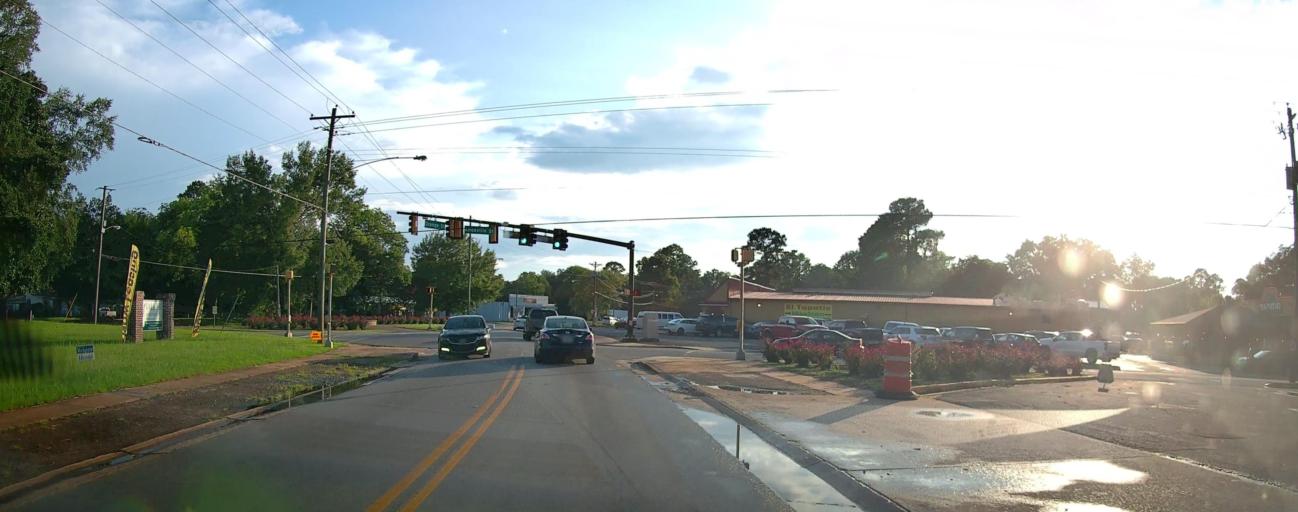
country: US
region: Georgia
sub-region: Peach County
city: Fort Valley
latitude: 32.5590
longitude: -83.8931
